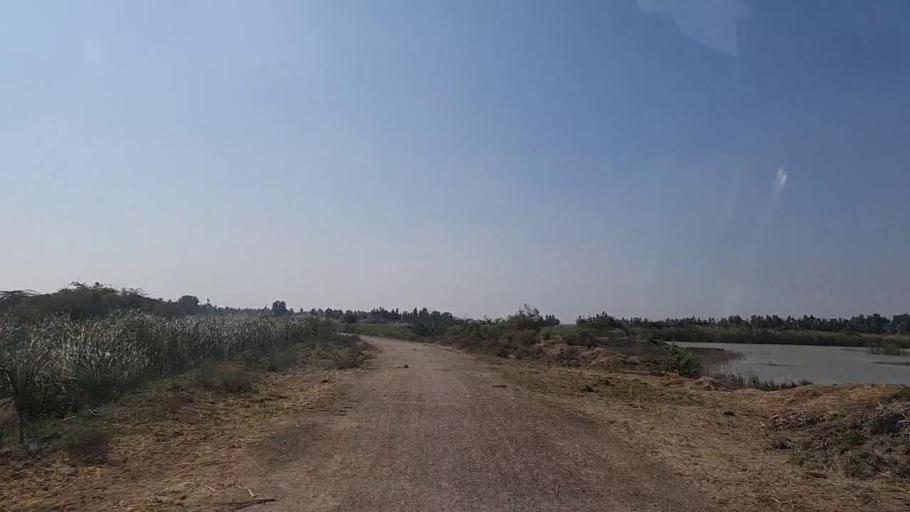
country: PK
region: Sindh
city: Thatta
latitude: 24.7853
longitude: 67.9322
